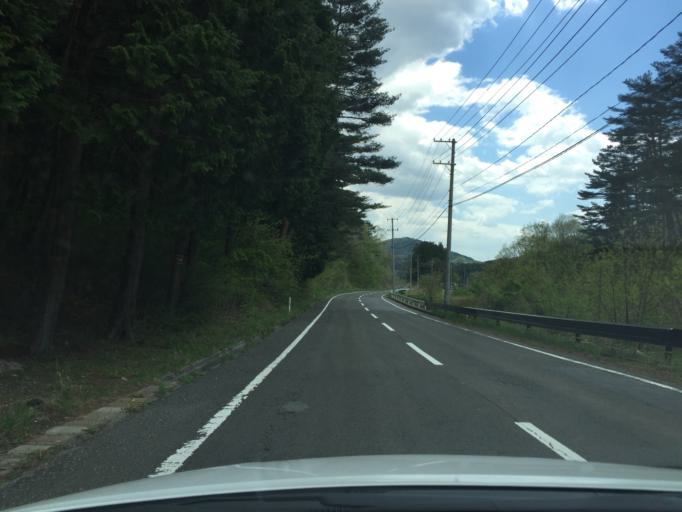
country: JP
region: Fukushima
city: Yanagawamachi-saiwaicho
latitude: 37.7245
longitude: 140.6864
